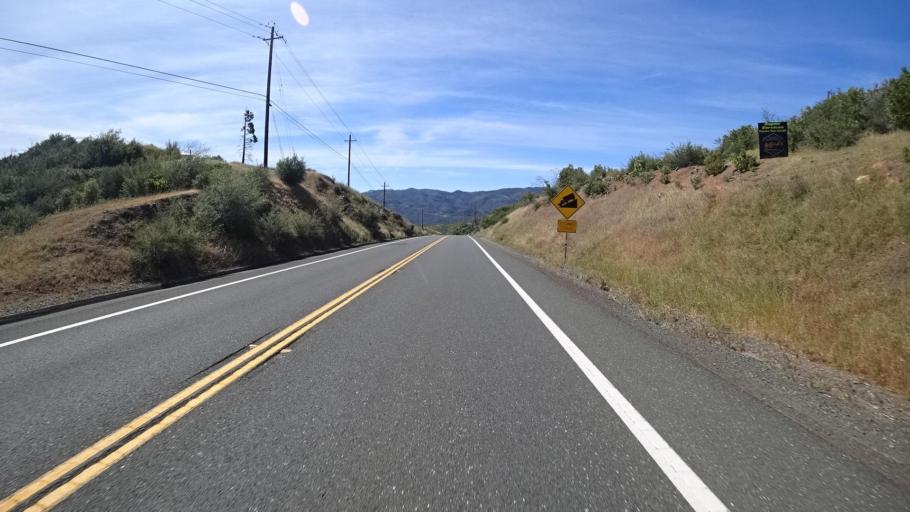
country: US
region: California
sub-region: Lake County
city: Cobb
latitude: 38.8008
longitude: -122.7052
